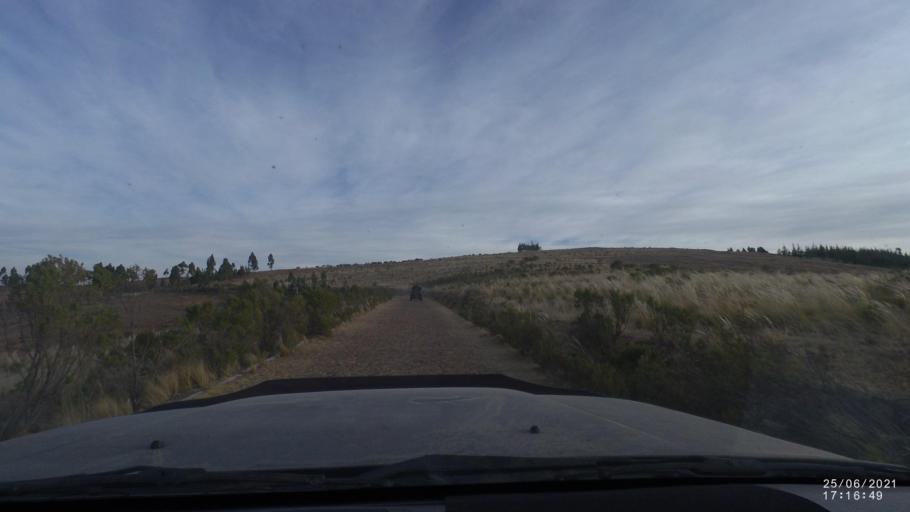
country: BO
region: Cochabamba
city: Arani
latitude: -17.8835
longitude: -65.7008
